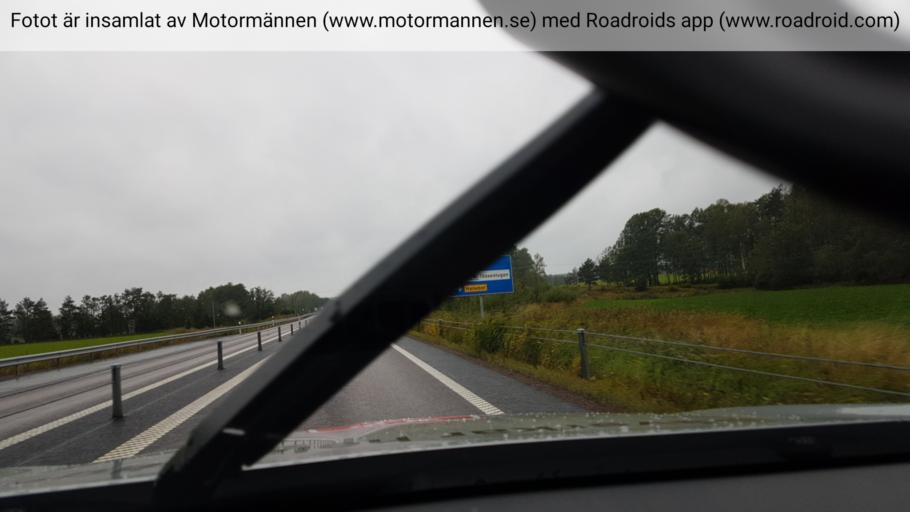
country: SE
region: Vaestra Goetaland
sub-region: Amals Kommun
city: Amal
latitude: 58.9700
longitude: 12.6192
